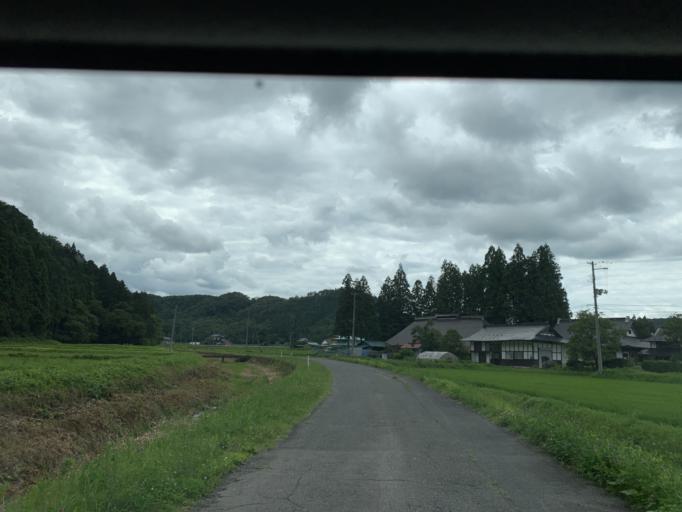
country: JP
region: Iwate
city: Ichinoseki
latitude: 38.9485
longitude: 141.0165
